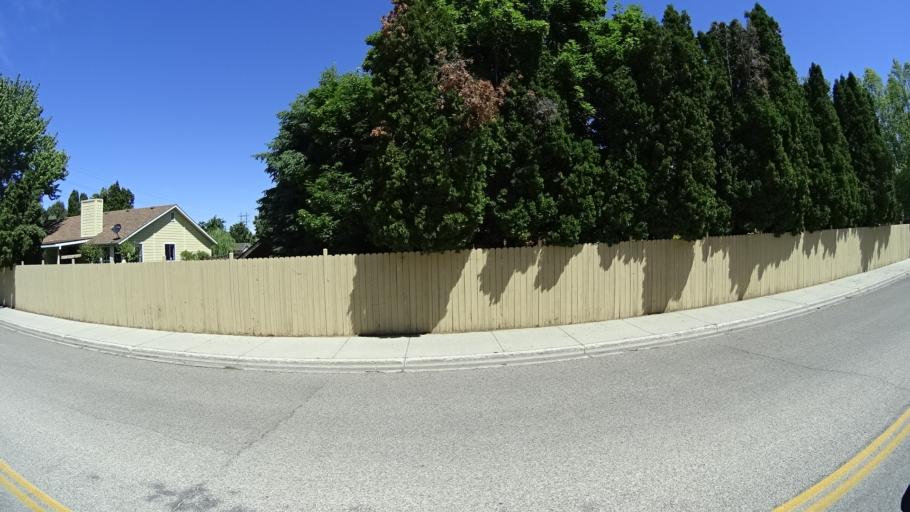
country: US
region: Idaho
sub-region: Ada County
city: Boise
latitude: 43.5678
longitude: -116.1578
